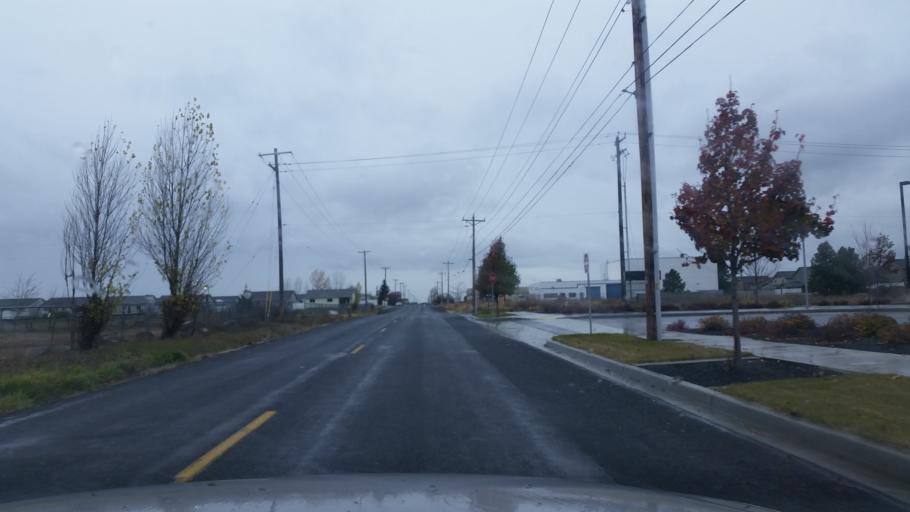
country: US
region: Washington
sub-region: Spokane County
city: Airway Heights
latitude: 47.5941
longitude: -117.5342
